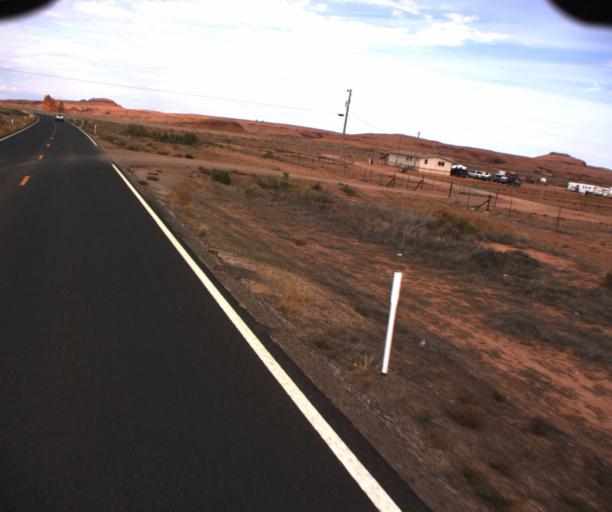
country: US
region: Arizona
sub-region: Apache County
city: Many Farms
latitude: 36.7355
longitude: -109.6338
